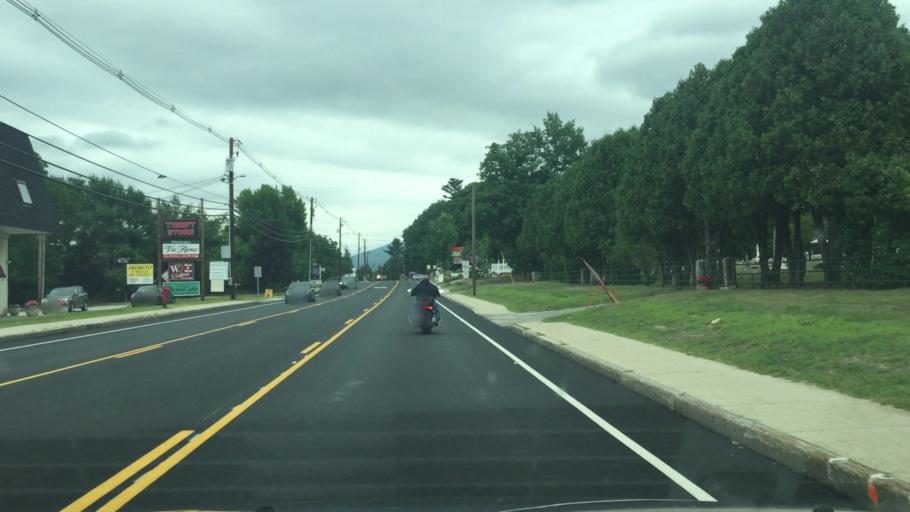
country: US
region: New Hampshire
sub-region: Carroll County
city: North Conway
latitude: 44.0361
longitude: -71.1220
